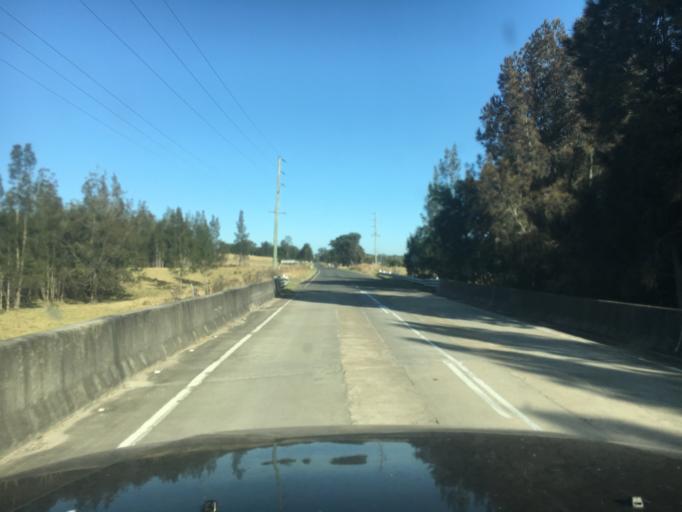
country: AU
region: New South Wales
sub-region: Singleton
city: Singleton
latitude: -32.5457
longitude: 151.2576
